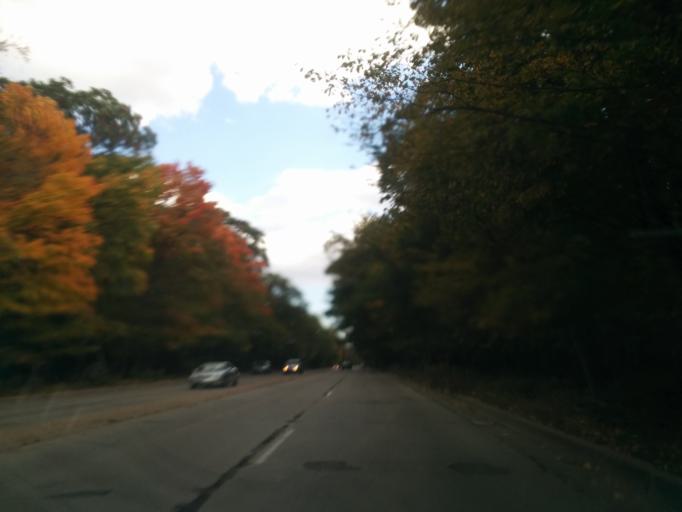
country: US
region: Illinois
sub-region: Cook County
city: Park Ridge
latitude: 41.9943
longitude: -87.8540
